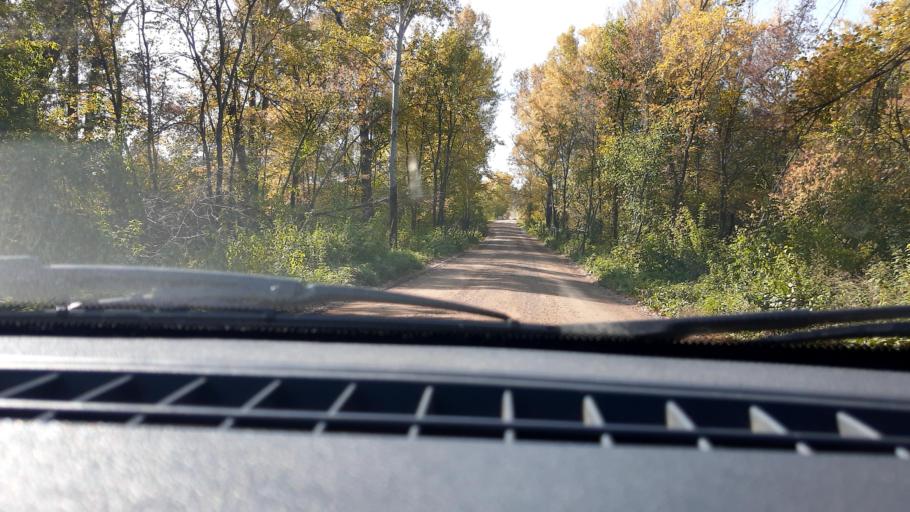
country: RU
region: Bashkortostan
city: Mikhaylovka
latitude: 54.7388
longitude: 55.8399
